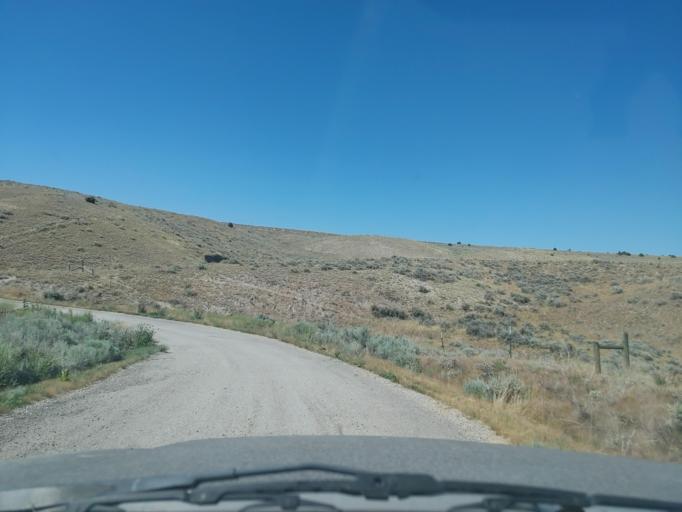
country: US
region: Montana
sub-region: Ravalli County
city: Stevensville
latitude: 46.3608
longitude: -114.0371
